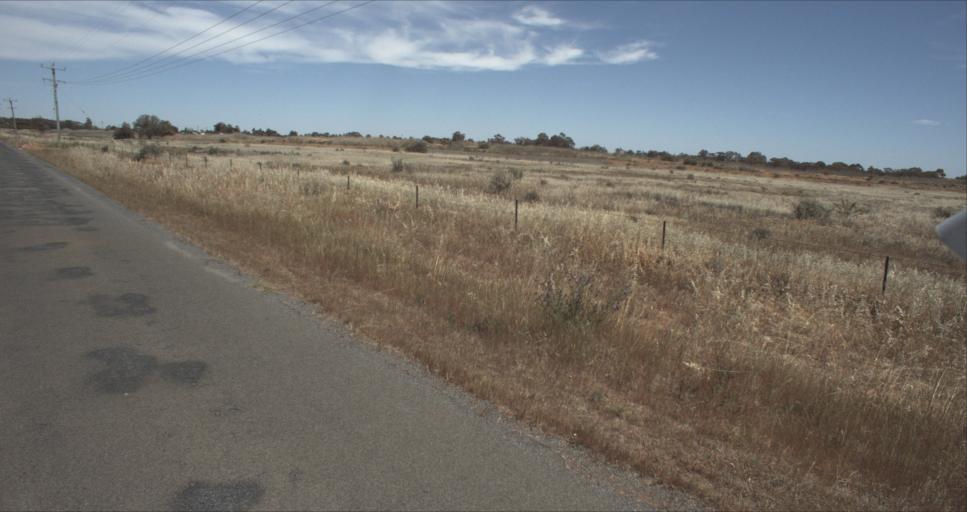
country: AU
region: New South Wales
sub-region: Leeton
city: Leeton
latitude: -34.6053
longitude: 146.4262
